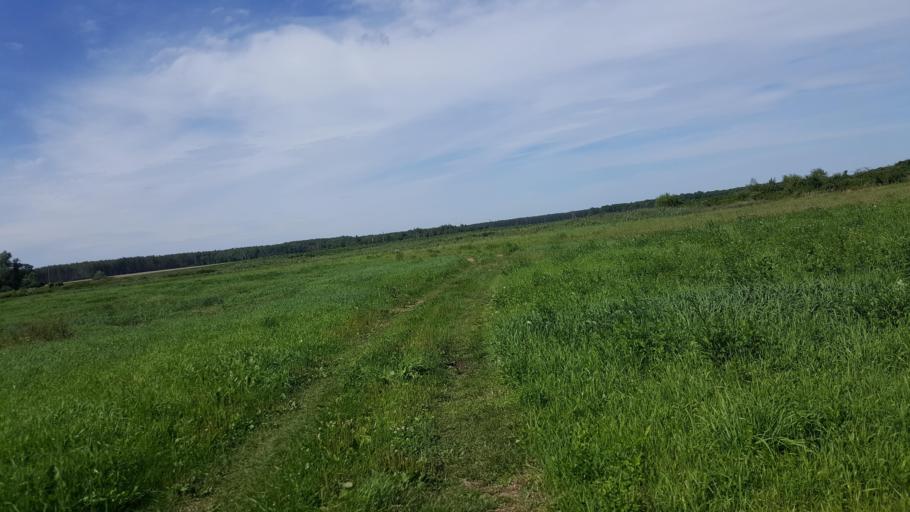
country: BY
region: Brest
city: Zhabinka
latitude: 52.4645
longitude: 24.1038
